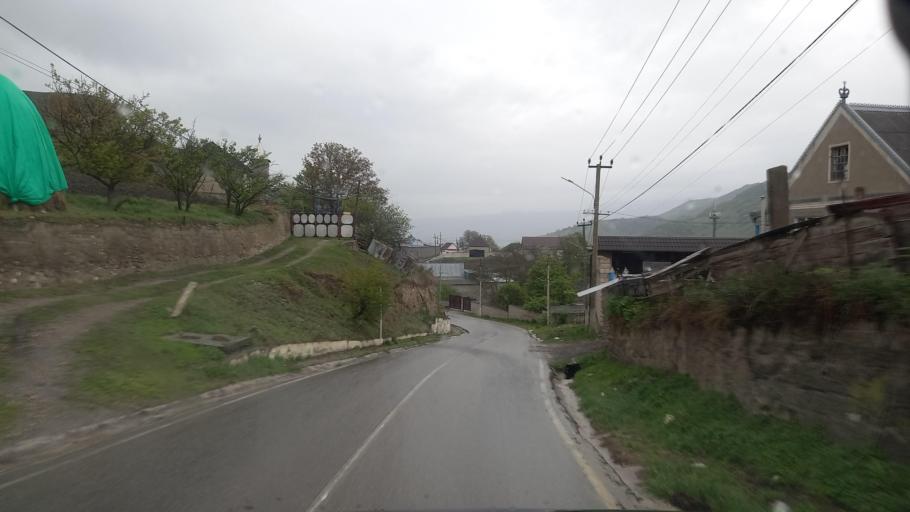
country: RU
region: Kabardino-Balkariya
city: Gundelen
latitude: 43.6000
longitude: 43.1529
